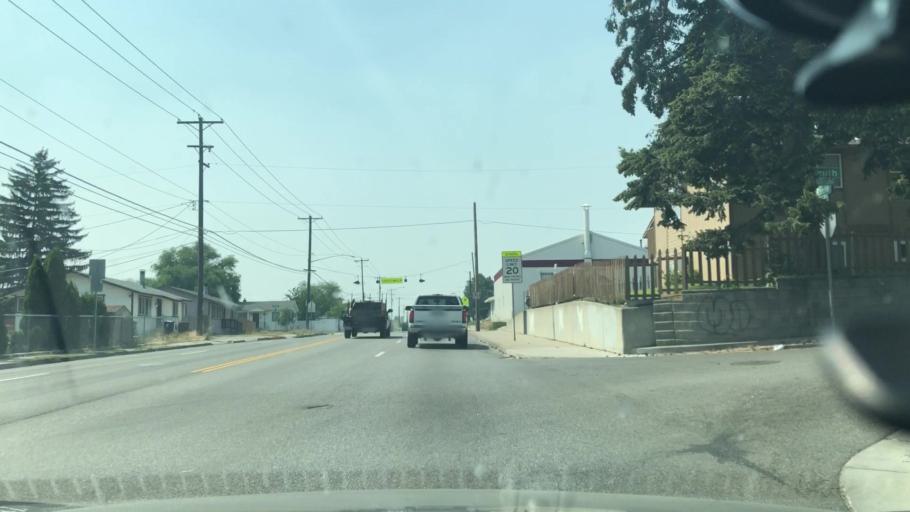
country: US
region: Washington
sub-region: Spokane County
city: Spokane
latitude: 47.6862
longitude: -117.3722
